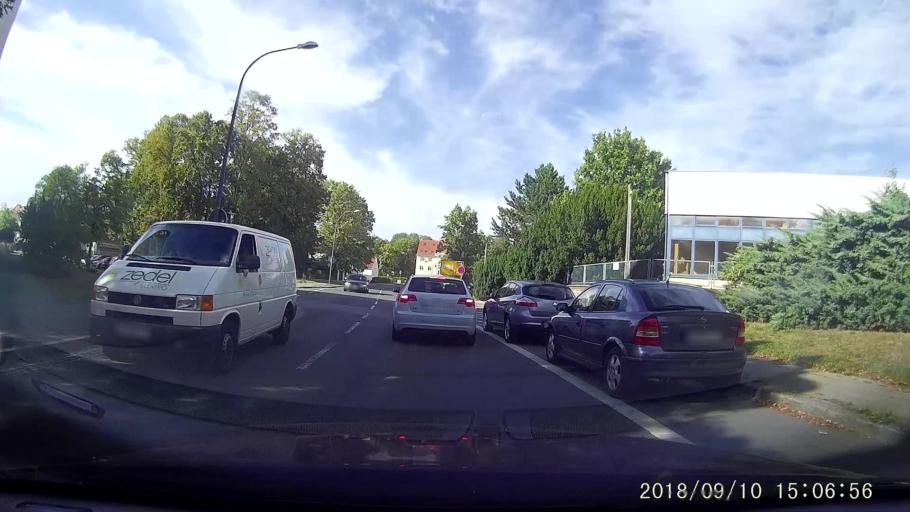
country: DE
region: Saxony
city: Goerlitz
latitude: 51.1468
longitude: 14.9485
